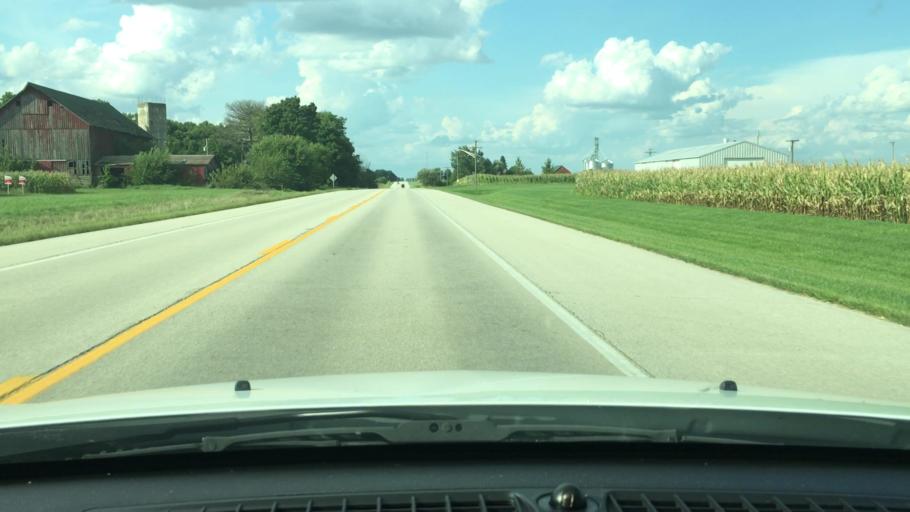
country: US
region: Illinois
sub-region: DeKalb County
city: Waterman
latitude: 41.7742
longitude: -88.7542
